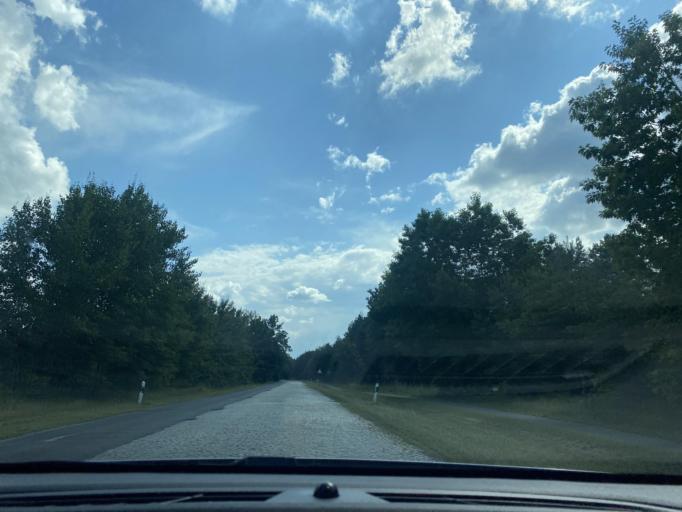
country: DE
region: Saxony
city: Boxberg
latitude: 51.4194
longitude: 14.5895
